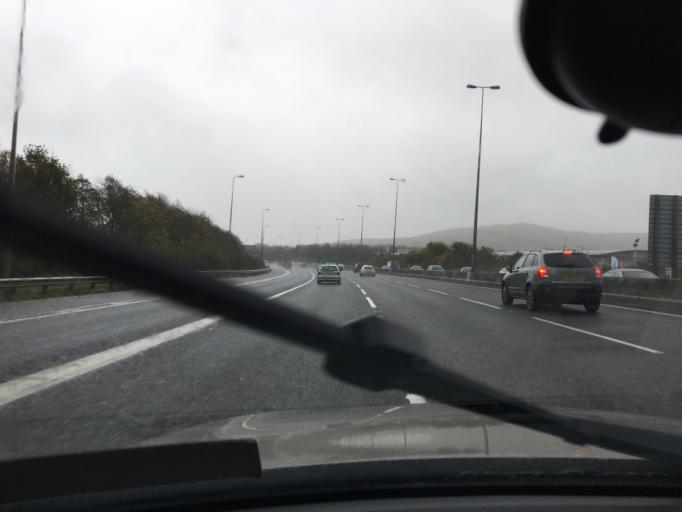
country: GB
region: Northern Ireland
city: Carnmoney
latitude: 54.6727
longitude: -5.9736
